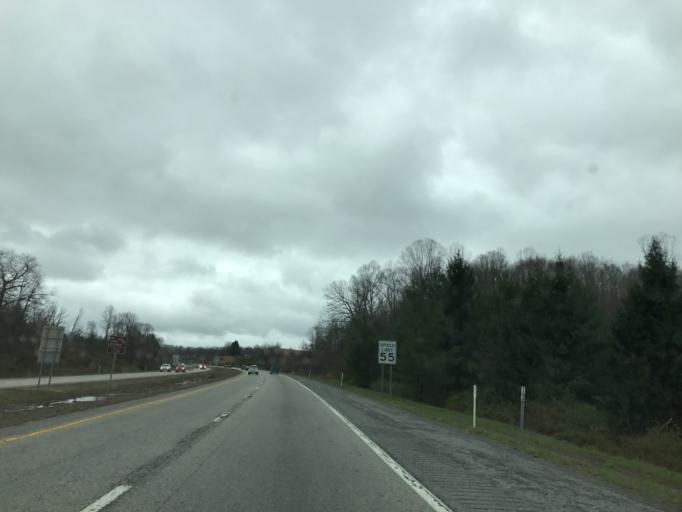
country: US
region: West Virginia
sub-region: Fayette County
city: Fayetteville
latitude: 38.0463
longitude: -81.1213
